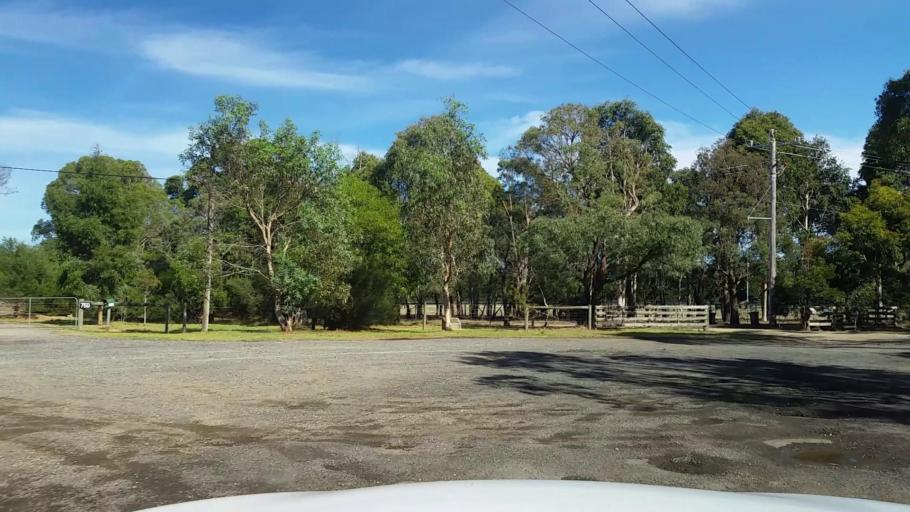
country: AU
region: Victoria
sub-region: Mornington Peninsula
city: Baxter
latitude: -38.2040
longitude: 145.1545
